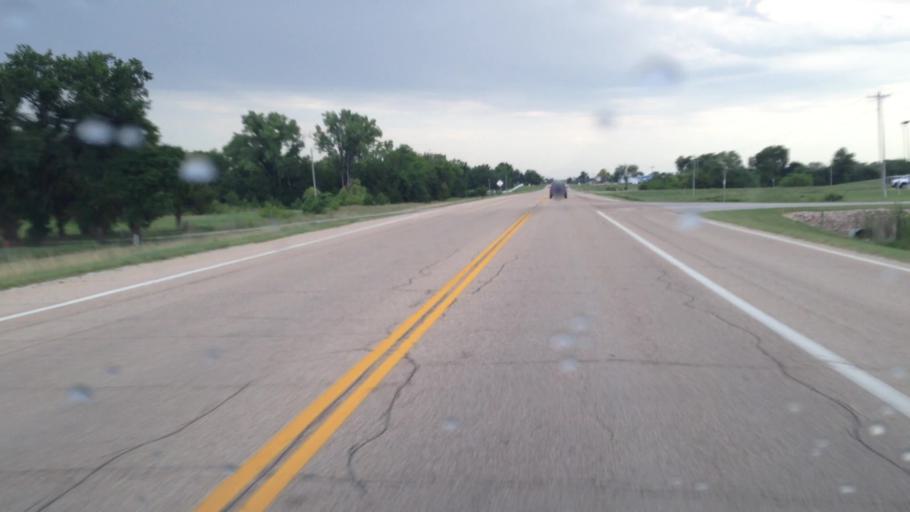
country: US
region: Kansas
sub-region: Coffey County
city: Burlington
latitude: 38.1854
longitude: -95.7387
